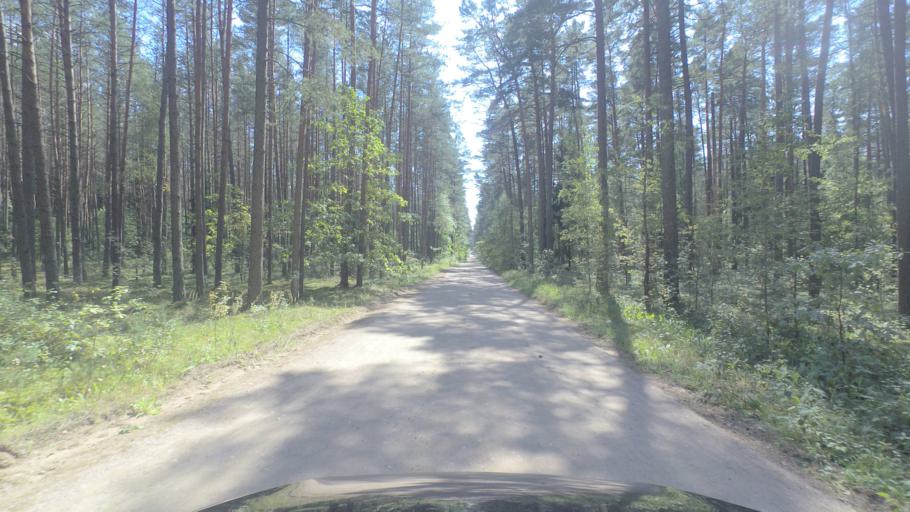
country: LT
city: Nemencine
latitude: 54.8469
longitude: 25.4978
